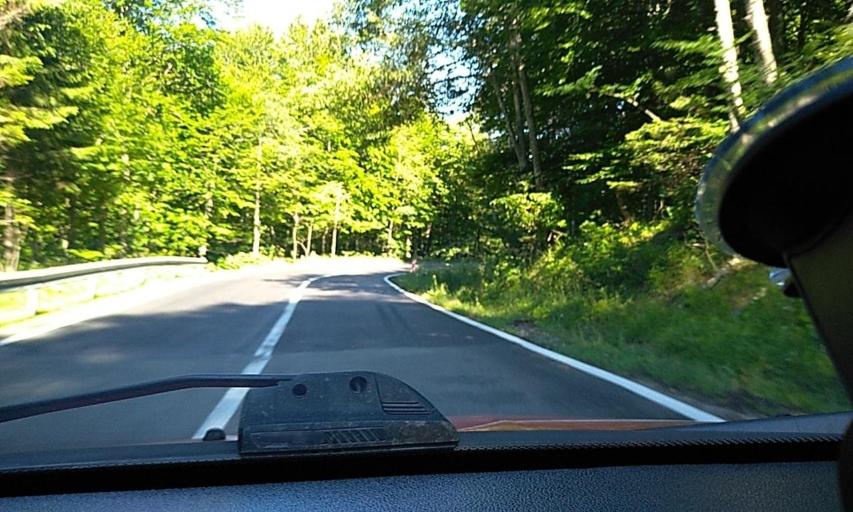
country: RO
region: Brasov
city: Crivina
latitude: 45.4983
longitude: 25.8583
